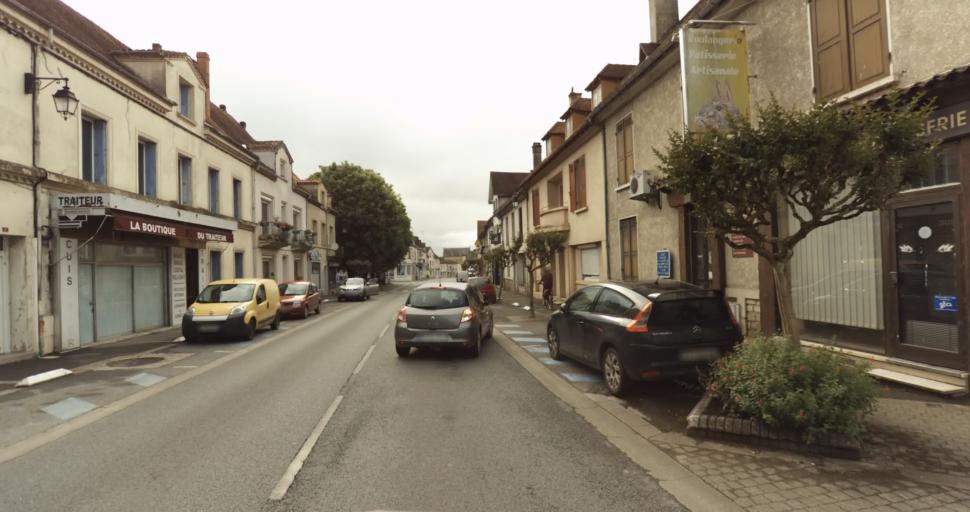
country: FR
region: Aquitaine
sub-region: Departement de la Dordogne
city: Mouleydier
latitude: 44.8551
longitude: 0.5931
